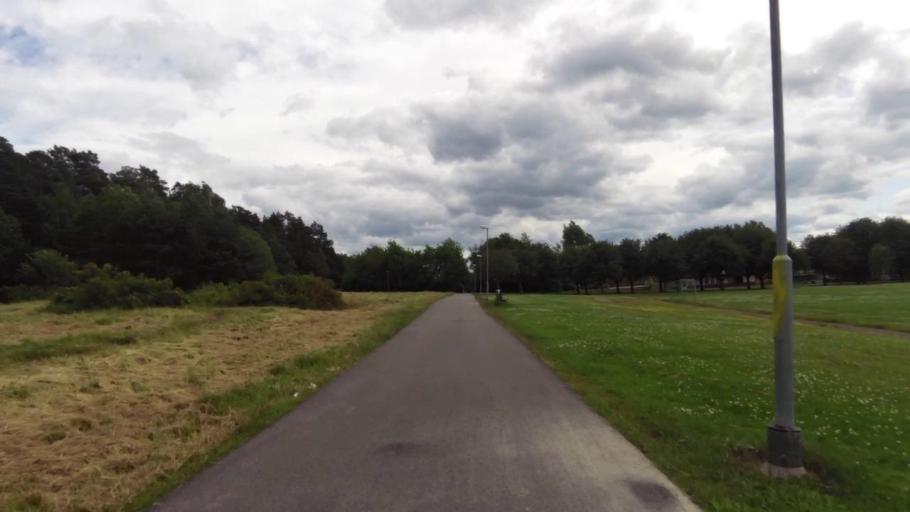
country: SE
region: OEstergoetland
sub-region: Linkopings Kommun
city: Linkoping
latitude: 58.4108
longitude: 15.5725
